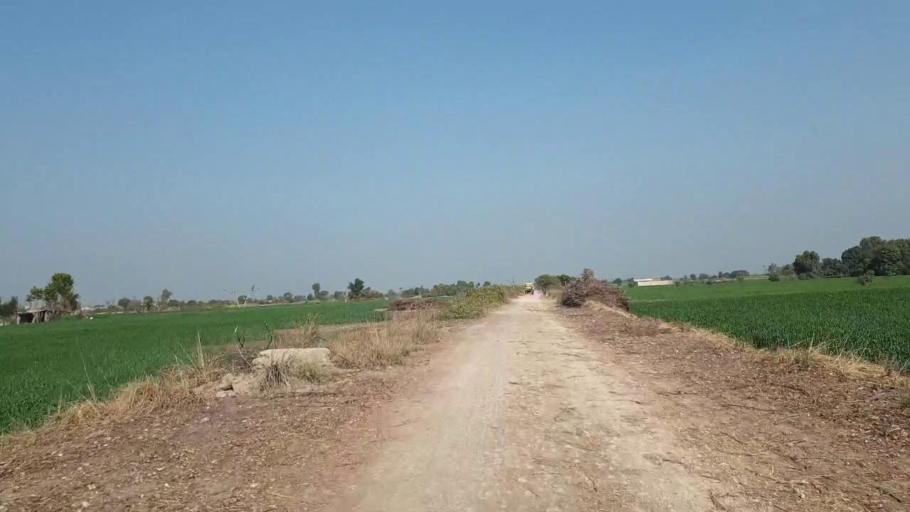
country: PK
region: Sindh
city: Hala
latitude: 25.9183
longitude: 68.4197
